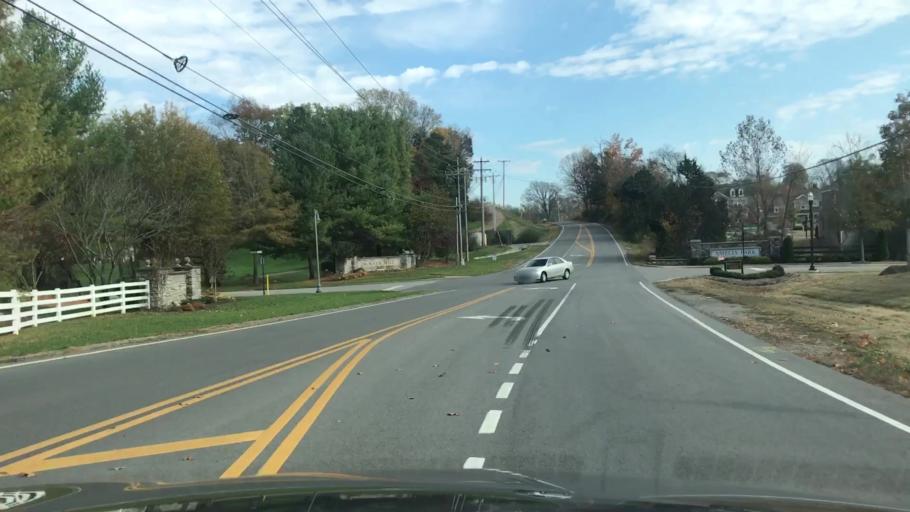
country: US
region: Tennessee
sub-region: Williamson County
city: Franklin
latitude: 35.9206
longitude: -86.7806
